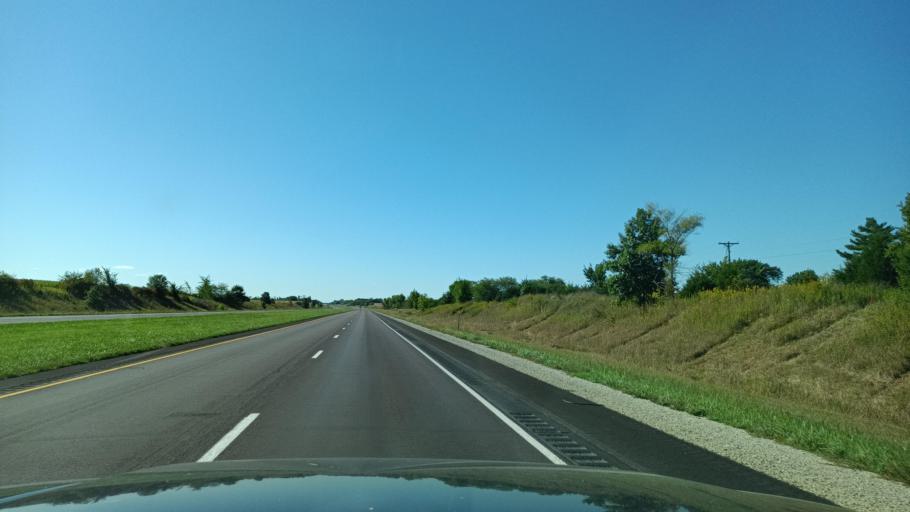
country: US
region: Illinois
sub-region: Hancock County
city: Nauvoo
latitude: 40.5012
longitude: -91.4432
